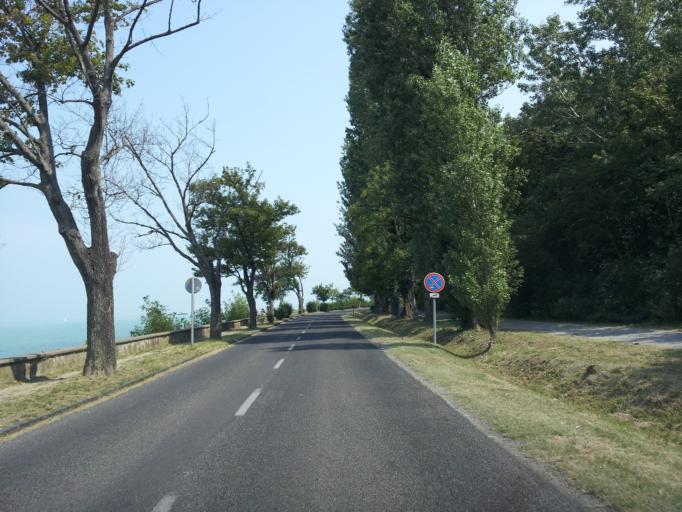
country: HU
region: Veszprem
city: Tihany
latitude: 46.9240
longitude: 17.8824
